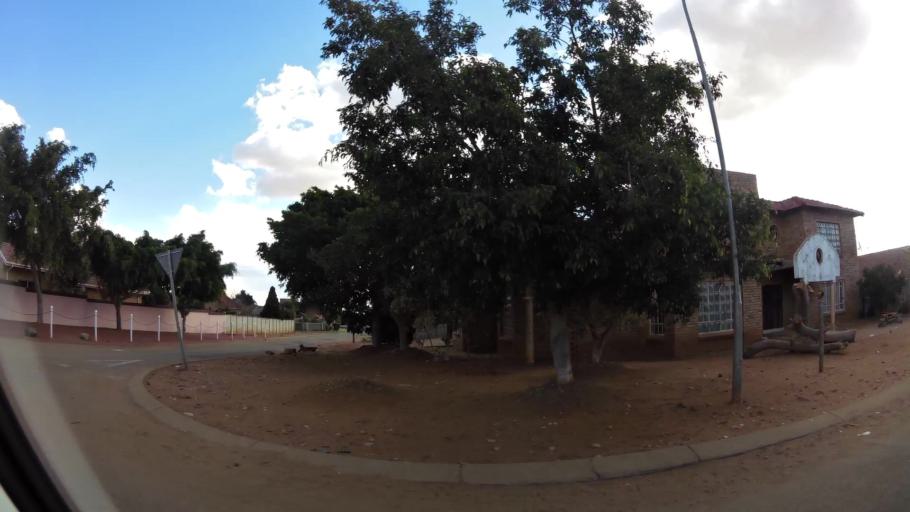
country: ZA
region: Limpopo
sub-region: Capricorn District Municipality
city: Polokwane
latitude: -23.9111
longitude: 29.4986
